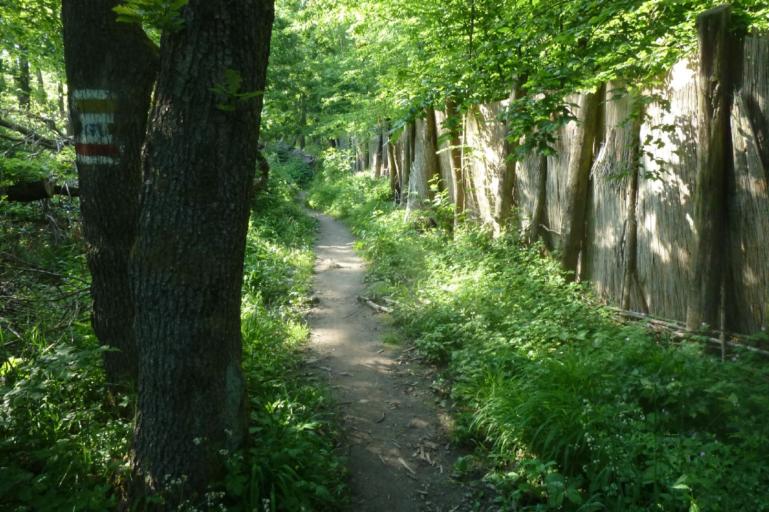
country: HU
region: Pest
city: Pilisszentkereszt
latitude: 47.7137
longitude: 18.8966
